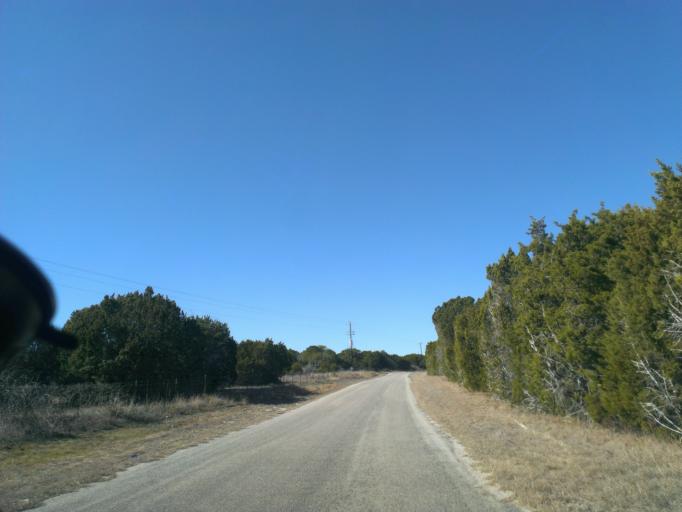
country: US
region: Texas
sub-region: Lampasas County
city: Lampasas
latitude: 30.9191
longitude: -98.1305
